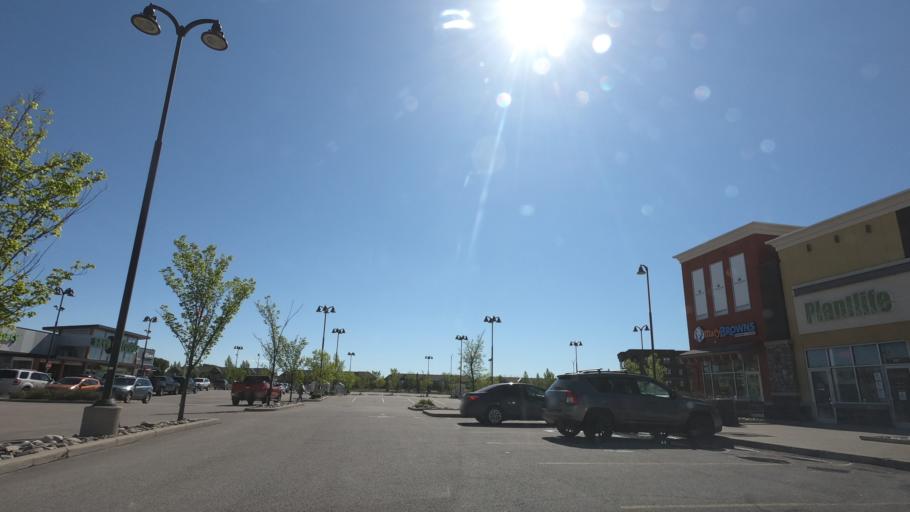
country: CA
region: Alberta
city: Airdrie
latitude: 51.2696
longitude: -113.9923
